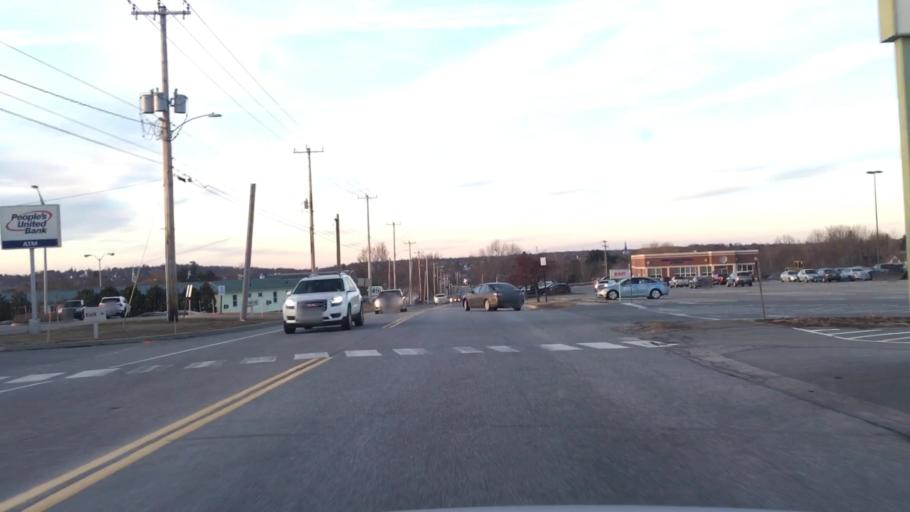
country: US
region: Maine
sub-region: Penobscot County
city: Brewer
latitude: 44.7856
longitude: -68.7529
